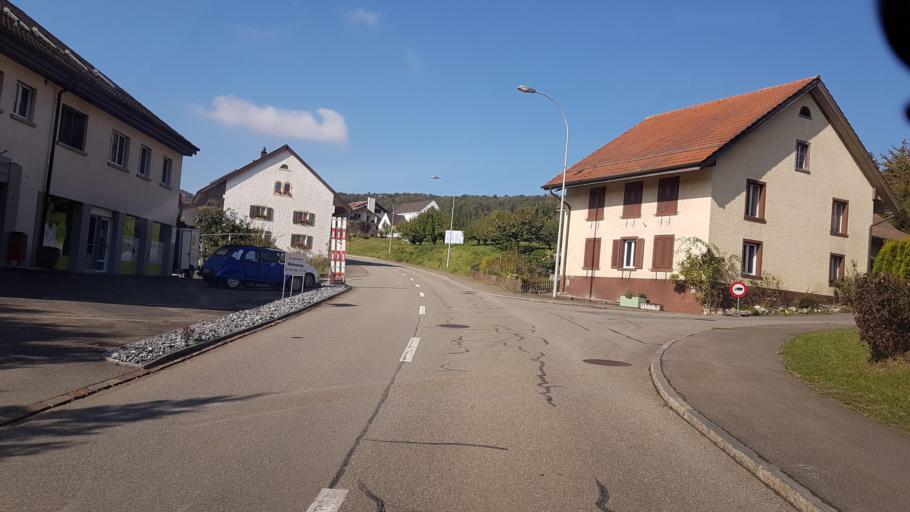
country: CH
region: Aargau
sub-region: Bezirk Laufenburg
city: Sulz
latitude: 47.5183
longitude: 8.1428
